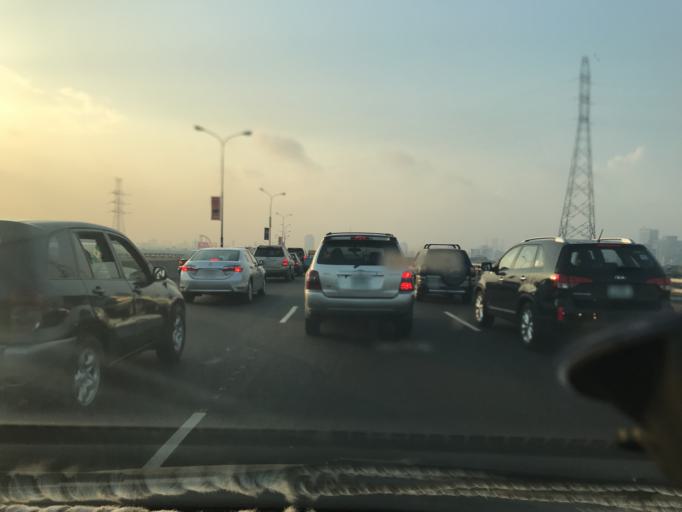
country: NG
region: Lagos
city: Lagos
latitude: 6.4684
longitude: 3.3910
